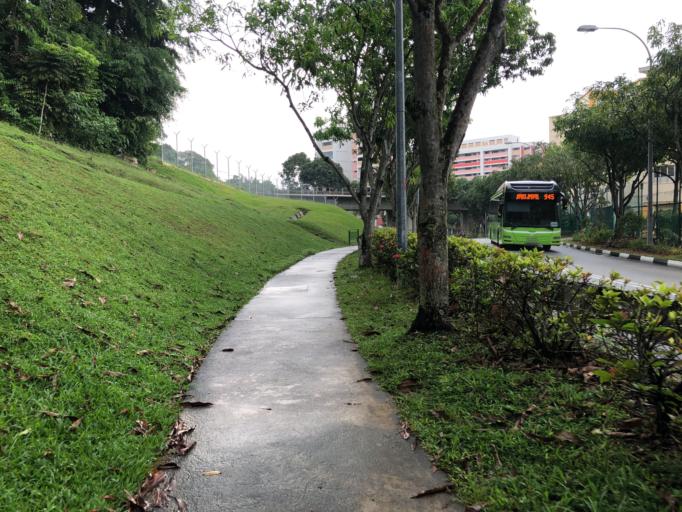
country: MY
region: Johor
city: Johor Bahru
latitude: 1.3523
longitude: 103.7529
